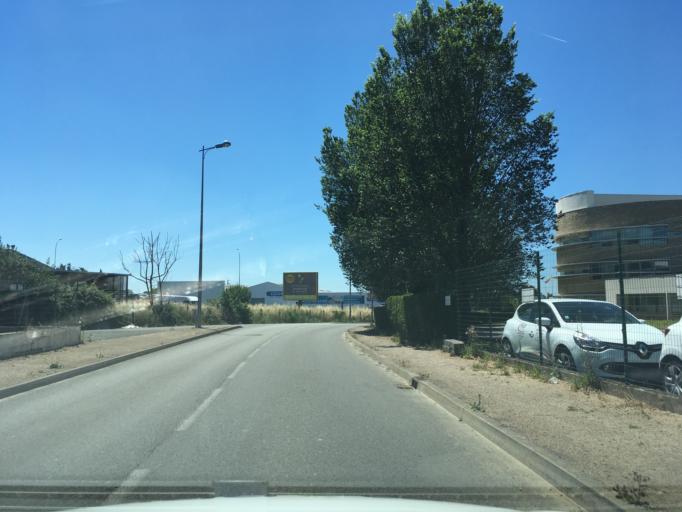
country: FR
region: Poitou-Charentes
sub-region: Departement des Deux-Sevres
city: Aiffres
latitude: 46.3351
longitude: -0.4148
